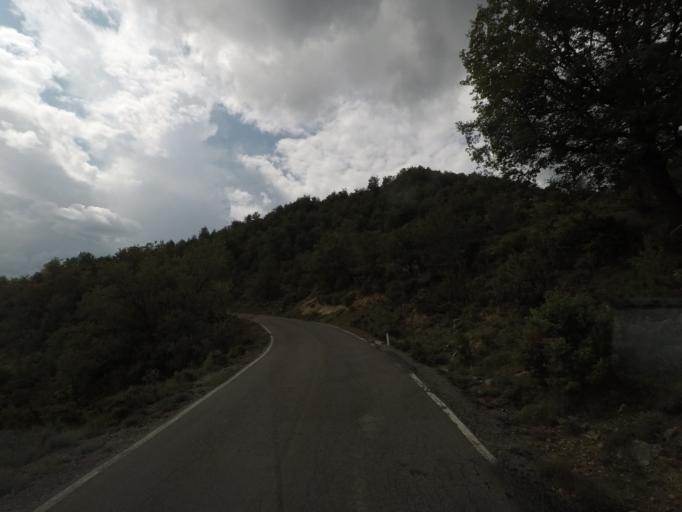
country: ES
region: Aragon
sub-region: Provincia de Huesca
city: Boltana
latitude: 42.4098
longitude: -0.0035
